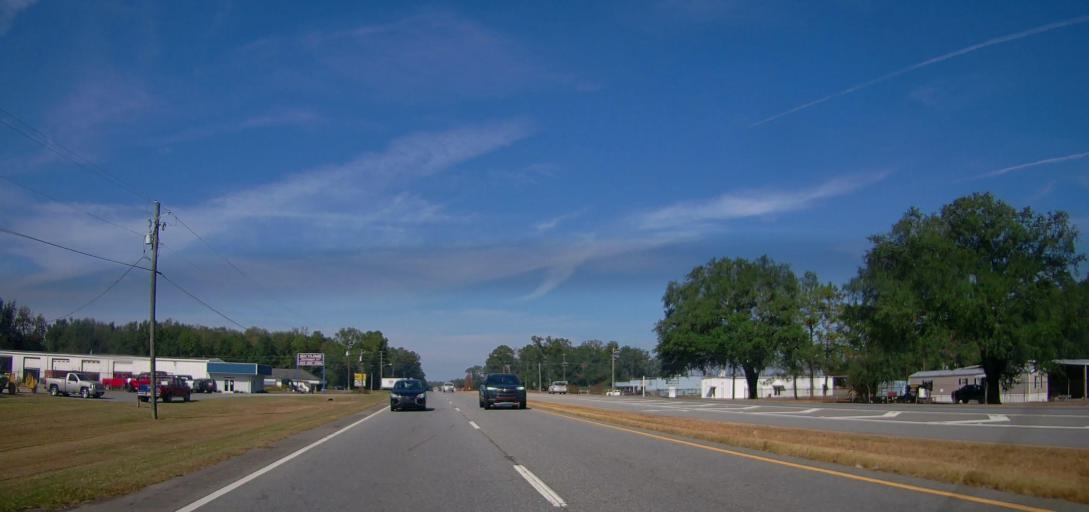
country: US
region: Georgia
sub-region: Dougherty County
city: Putney
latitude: 31.4817
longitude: -84.1170
